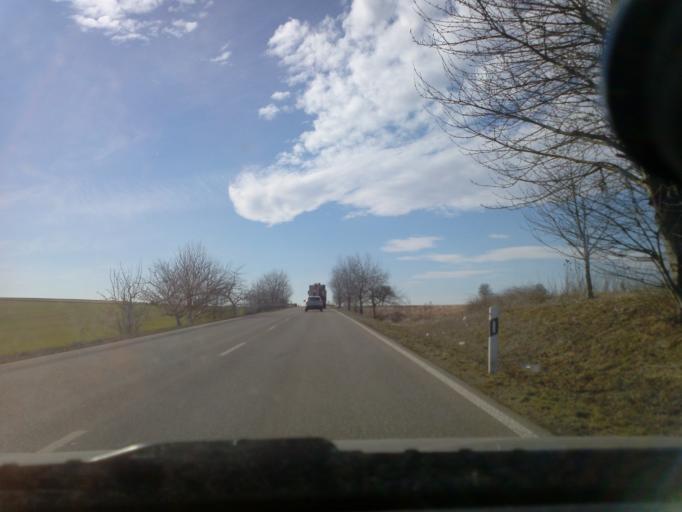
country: DE
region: Baden-Wuerttemberg
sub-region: Karlsruhe Region
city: Sulzfeld
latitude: 49.1219
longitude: 8.8511
